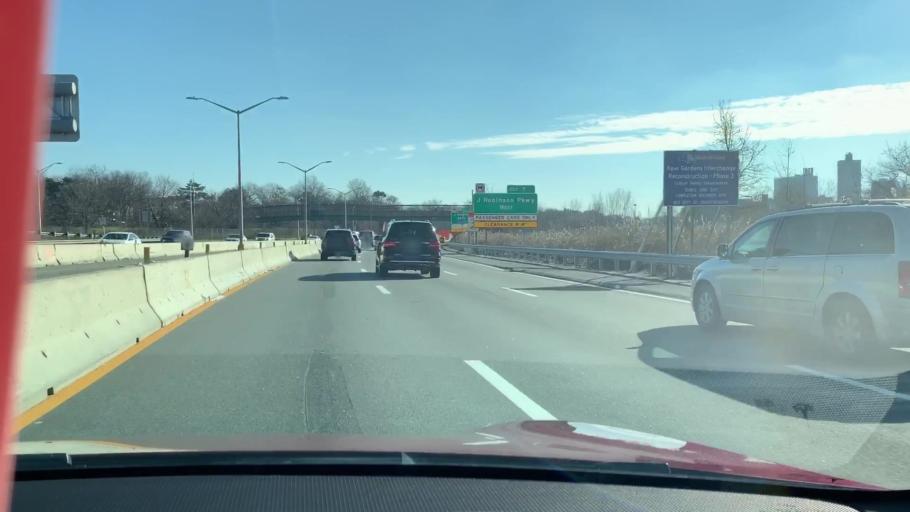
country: US
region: New York
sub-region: Queens County
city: Jamaica
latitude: 40.7241
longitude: -73.8289
